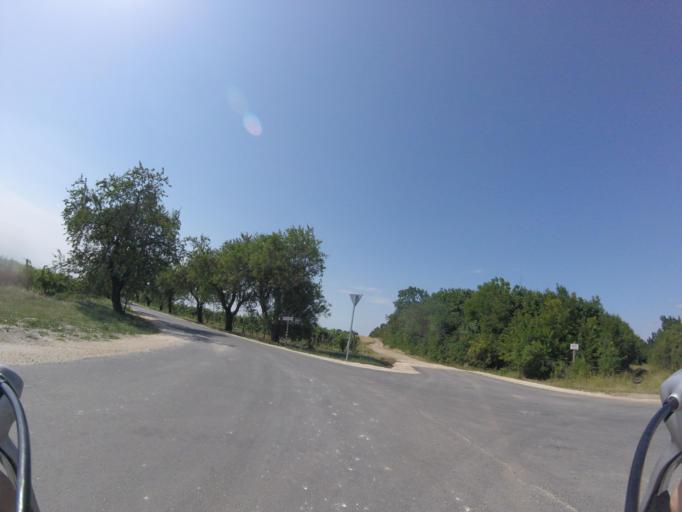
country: HU
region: Fejer
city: Etyek
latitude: 47.4240
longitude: 18.7272
